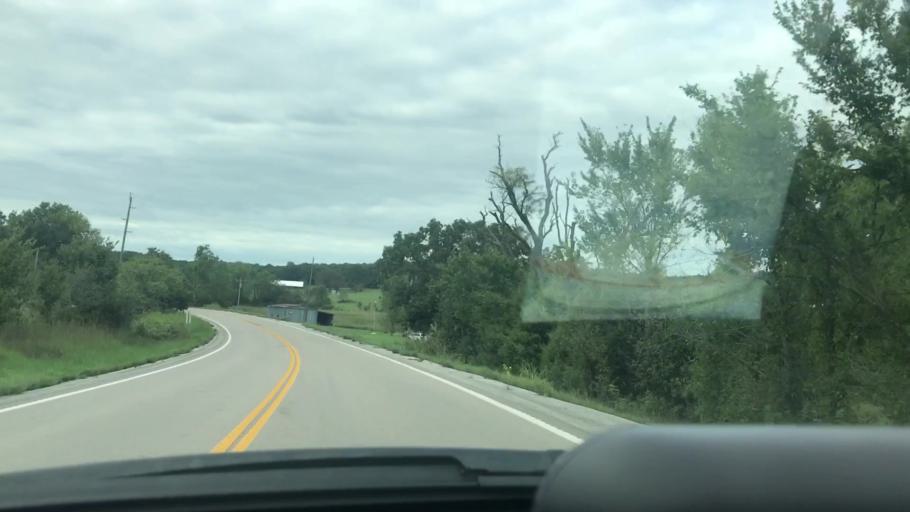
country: US
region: Missouri
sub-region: Benton County
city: Warsaw
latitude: 38.1323
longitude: -93.2802
